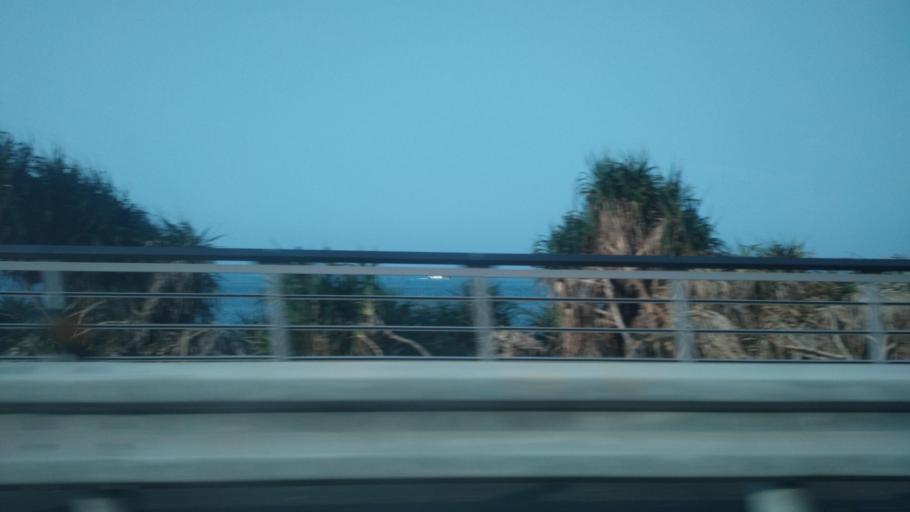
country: TW
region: Taiwan
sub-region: Keelung
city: Keelung
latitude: 25.2769
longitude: 121.6180
